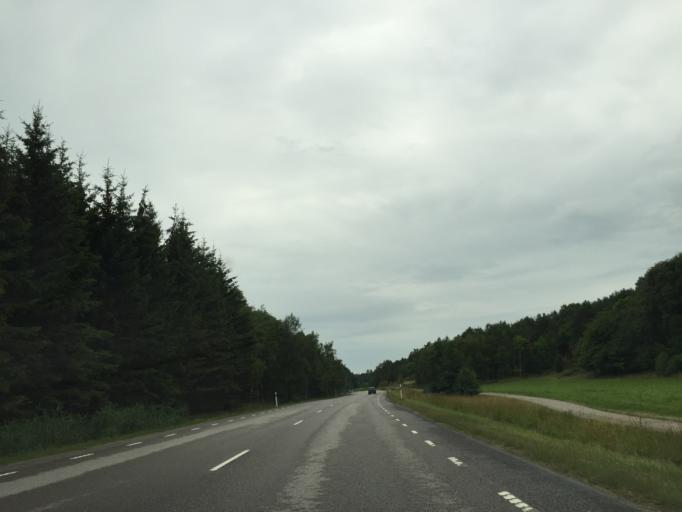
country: SE
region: Vaestra Goetaland
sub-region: Tjorns Kommun
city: Myggenas
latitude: 58.0234
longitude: 11.6873
